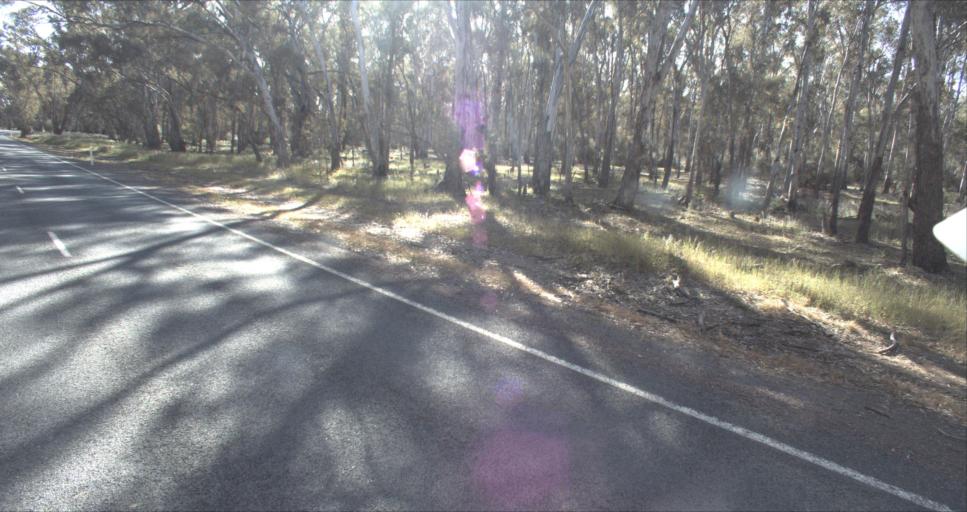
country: AU
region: New South Wales
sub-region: Leeton
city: Leeton
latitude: -34.6403
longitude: 146.3705
